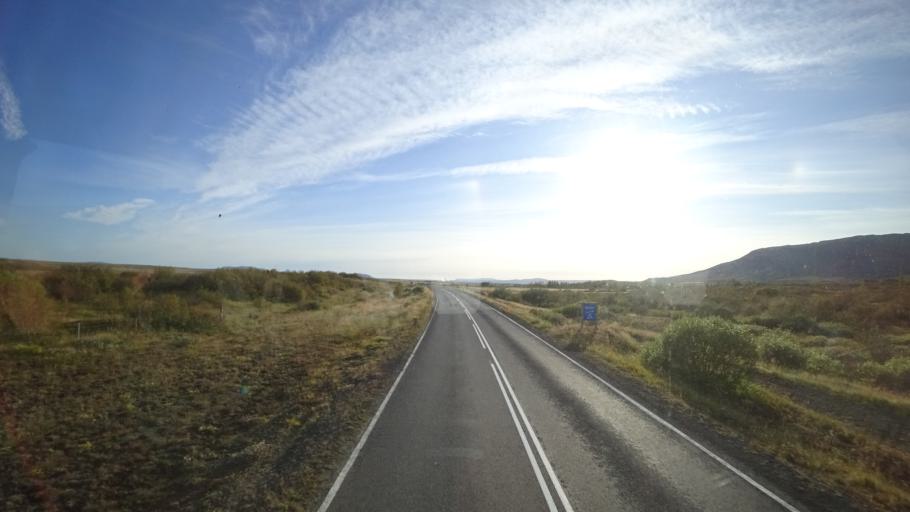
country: IS
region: South
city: Selfoss
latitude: 64.2528
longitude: -20.4883
